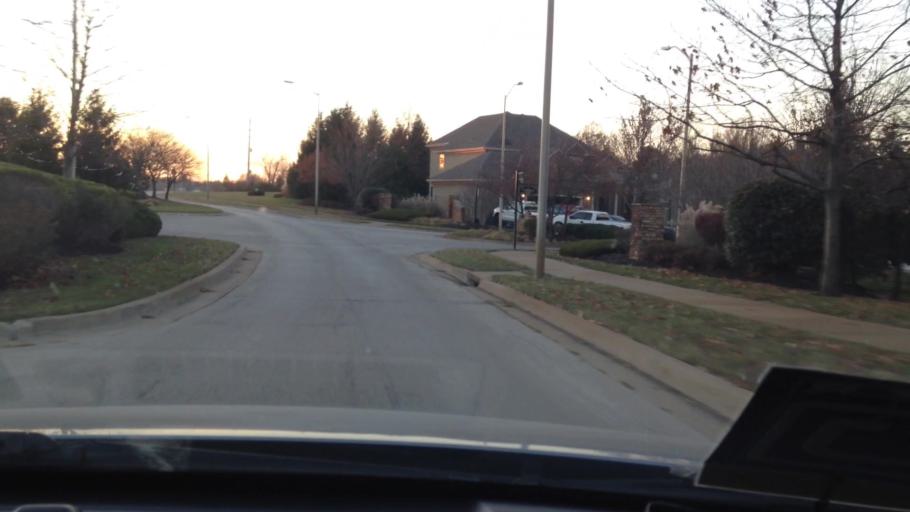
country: US
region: Missouri
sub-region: Clay County
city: Gladstone
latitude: 39.2847
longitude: -94.5554
